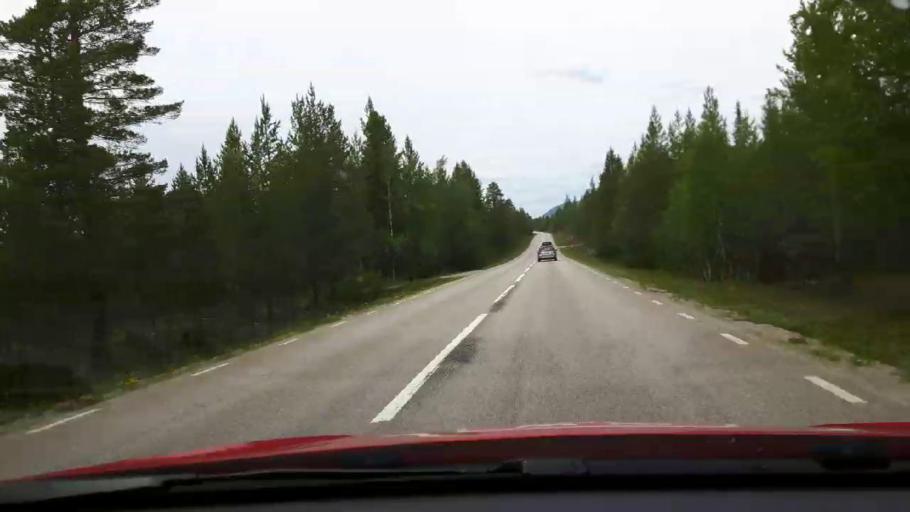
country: SE
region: Jaemtland
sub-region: Harjedalens Kommun
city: Sveg
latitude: 62.2318
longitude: 13.8561
